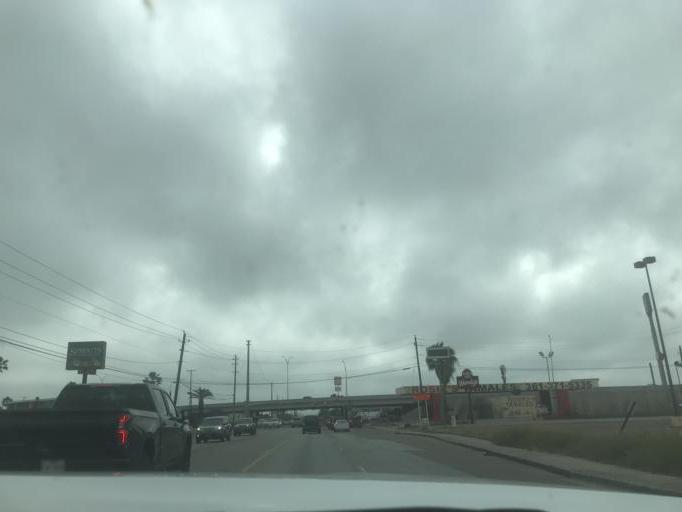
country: US
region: Texas
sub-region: Nueces County
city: Corpus Christi
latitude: 27.7058
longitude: -97.3628
